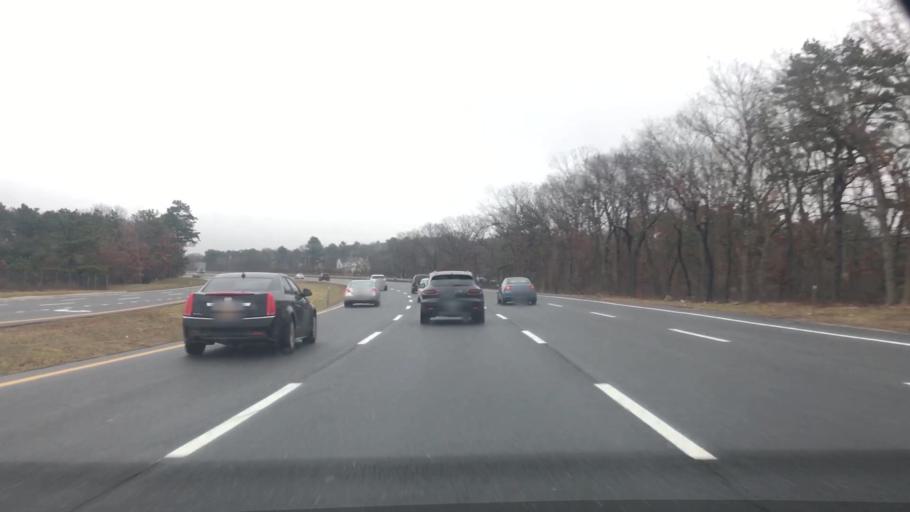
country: US
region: New York
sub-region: Suffolk County
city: Centereach
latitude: 40.8802
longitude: -73.1033
